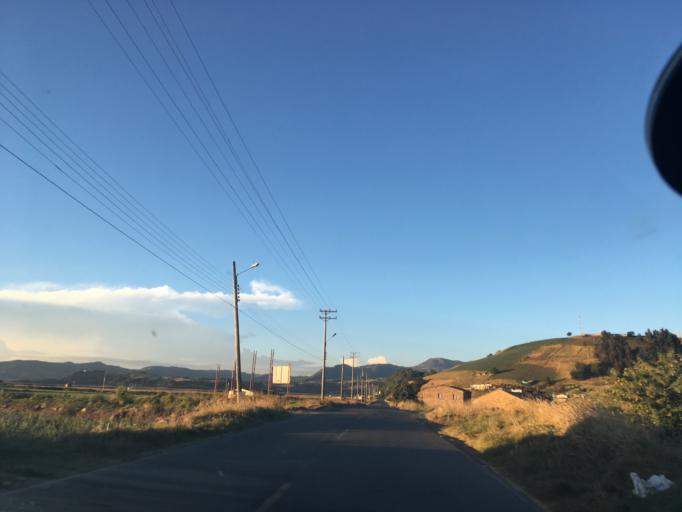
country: CO
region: Boyaca
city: Aquitania
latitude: 5.5311
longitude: -72.8842
